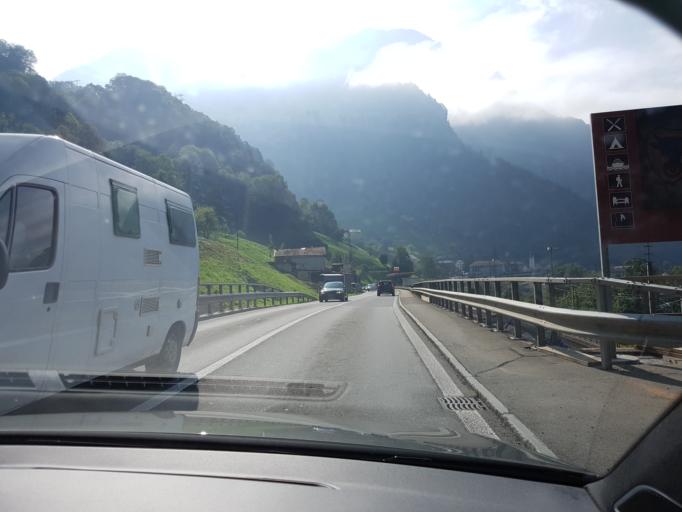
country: CH
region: Uri
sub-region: Uri
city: Bauen
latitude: 46.9551
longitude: 8.6200
